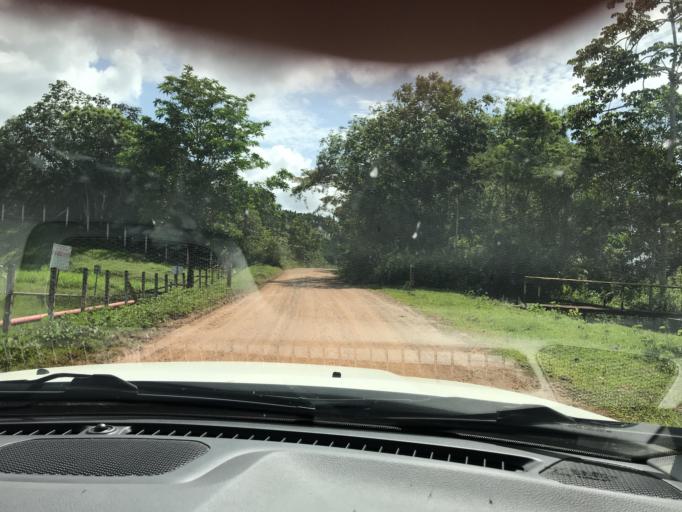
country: BR
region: Bahia
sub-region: Entre Rios
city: Entre Rios
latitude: -12.1689
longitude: -38.0677
